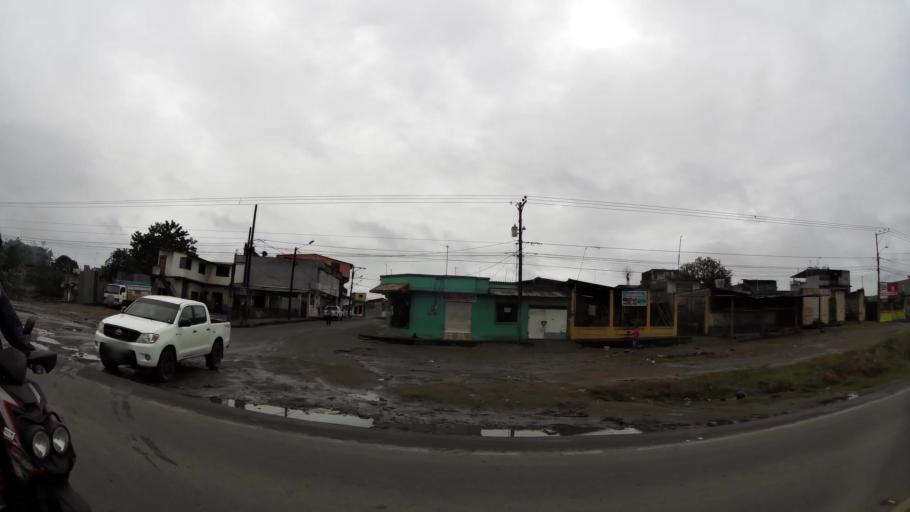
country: EC
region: Santo Domingo de los Tsachilas
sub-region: Canton Santo Domingo de los Colorados
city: Santo Domingo de los Colorados
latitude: -0.2621
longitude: -79.2024
